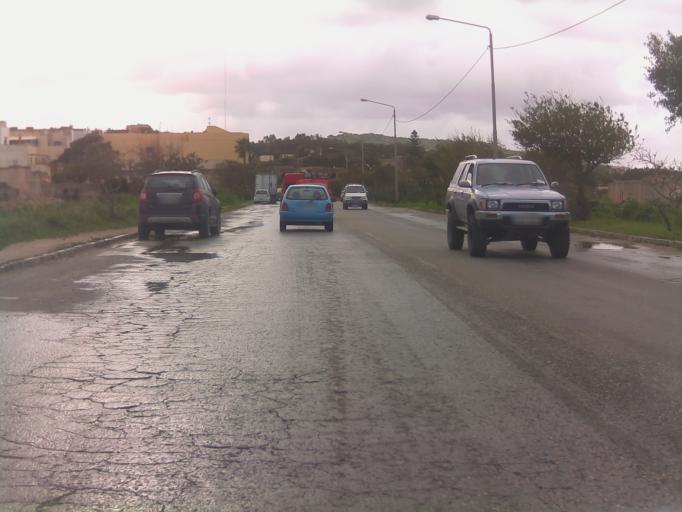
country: MT
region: Il-Mosta
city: Mosta
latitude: 35.9180
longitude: 14.4201
